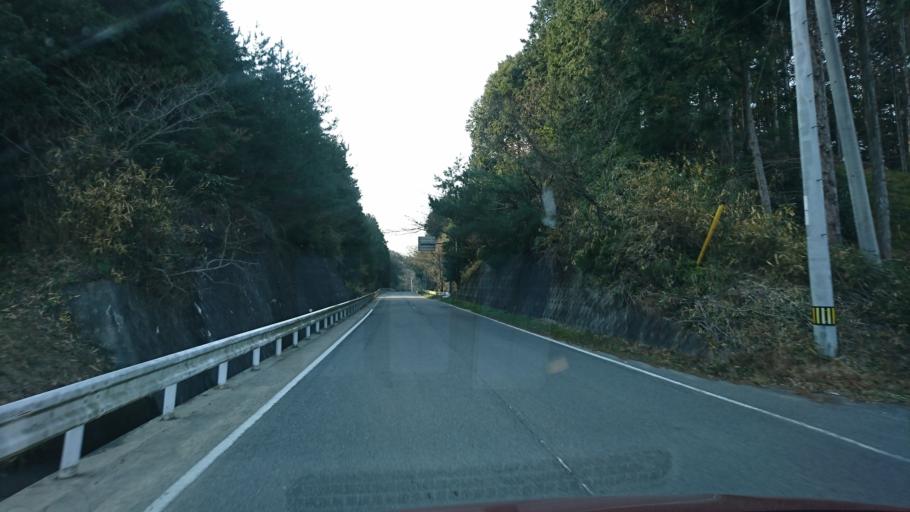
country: JP
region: Ehime
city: Hojo
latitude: 34.0199
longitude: 132.9745
